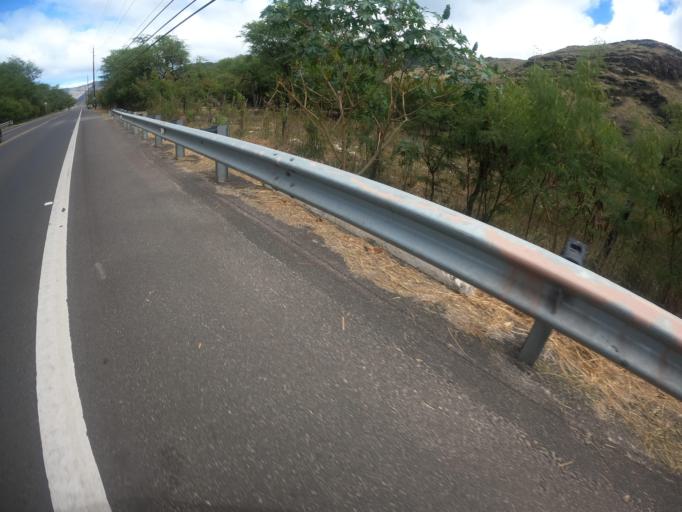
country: US
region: Hawaii
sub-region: Honolulu County
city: Makaha
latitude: 21.4950
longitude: -158.2286
